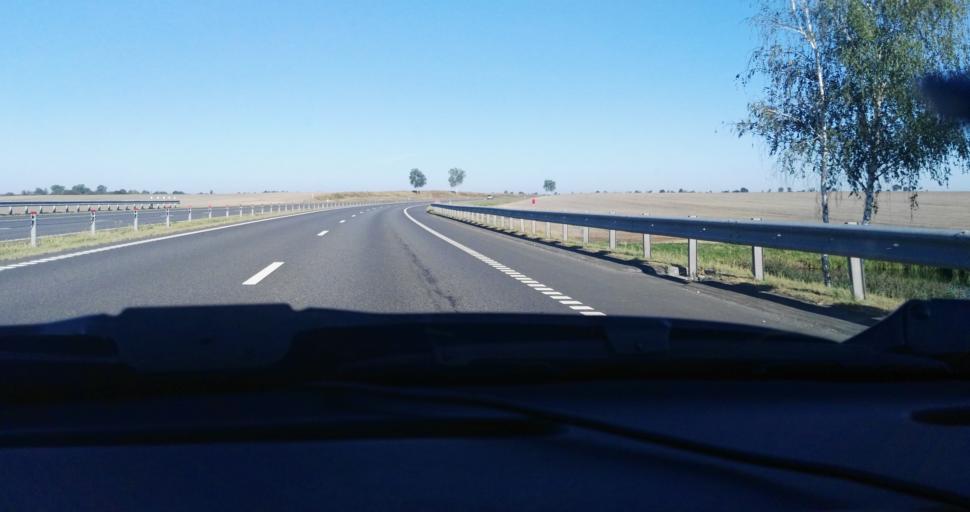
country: BY
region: Gomel
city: Buda-Kashalyova
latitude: 52.5070
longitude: 30.6378
